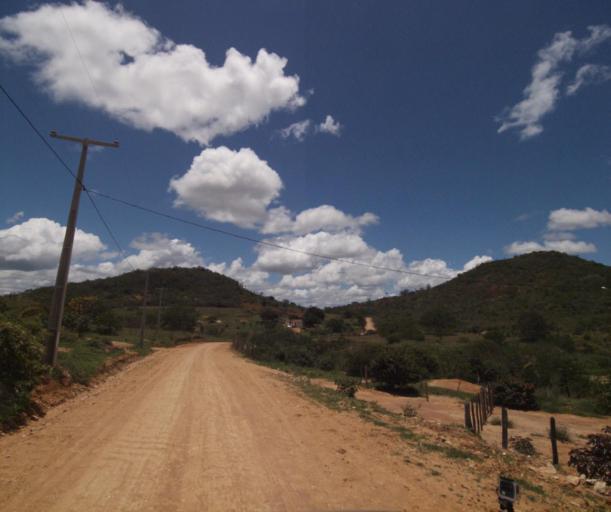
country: BR
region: Bahia
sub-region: Pocoes
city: Pocoes
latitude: -14.3796
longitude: -40.4098
